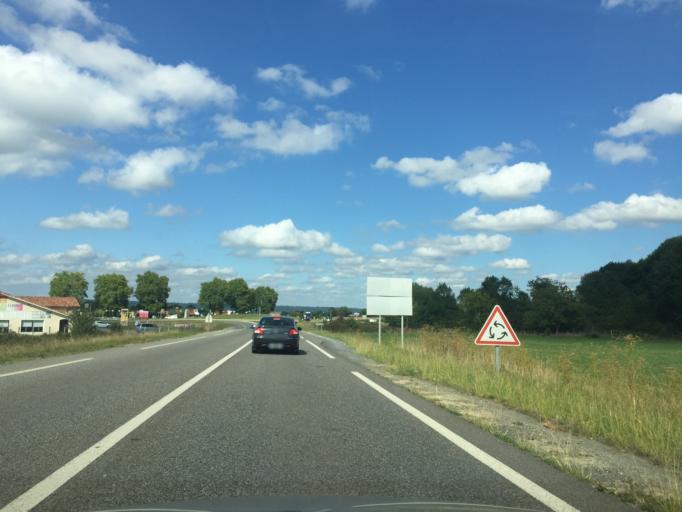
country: FR
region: Midi-Pyrenees
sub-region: Departement de la Haute-Garonne
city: Gourdan-Polignan
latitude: 43.0578
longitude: 0.5918
